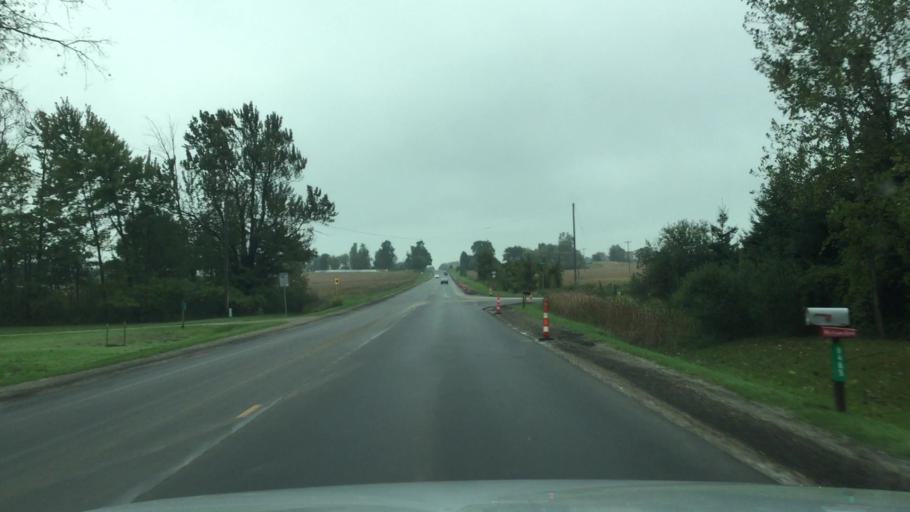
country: US
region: Michigan
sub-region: Shiawassee County
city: Perry
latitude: 42.8715
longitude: -84.2215
